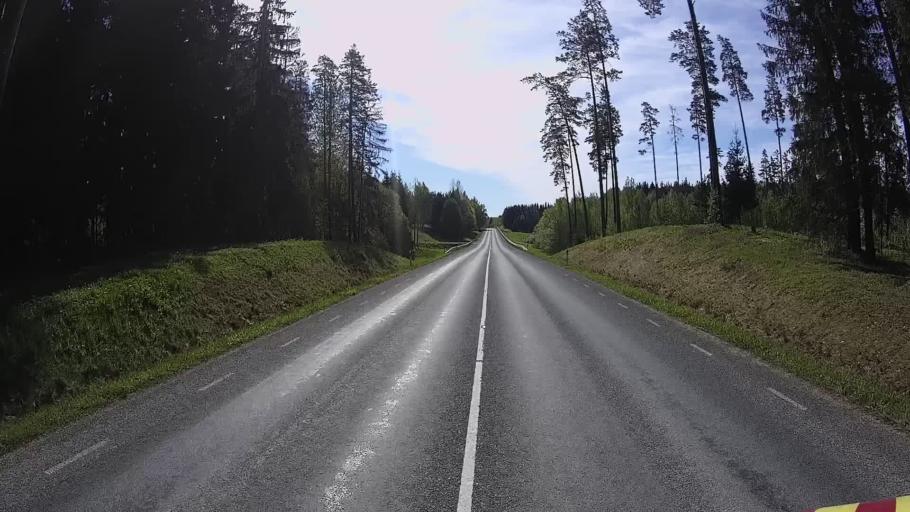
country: EE
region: Polvamaa
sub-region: Polva linn
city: Polva
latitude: 58.1623
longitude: 27.1569
